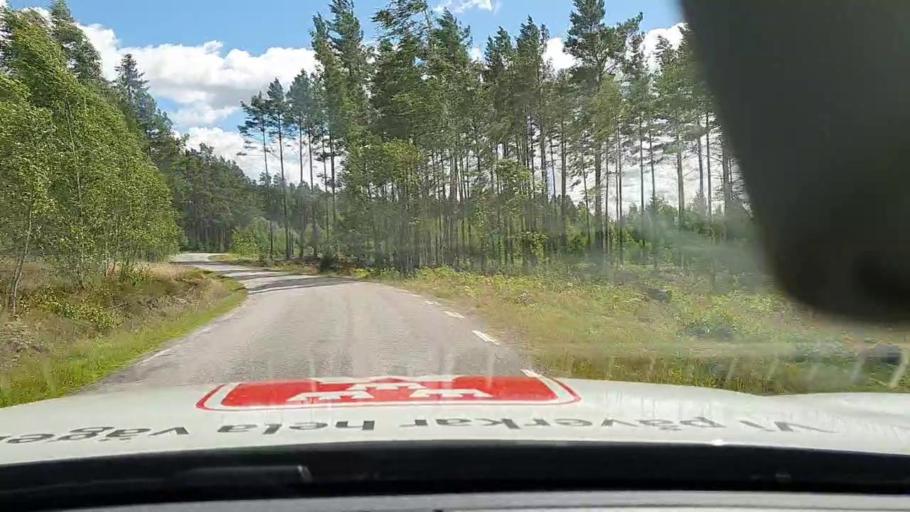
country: SE
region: Vaestra Goetaland
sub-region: Toreboda Kommun
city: Toereboda
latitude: 58.5807
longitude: 14.1224
